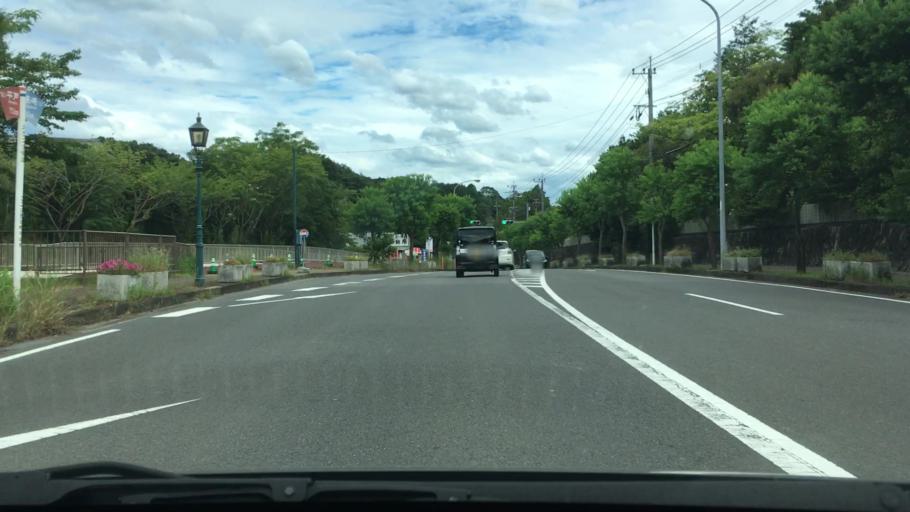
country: JP
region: Nagasaki
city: Sasebo
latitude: 32.9922
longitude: 129.7614
